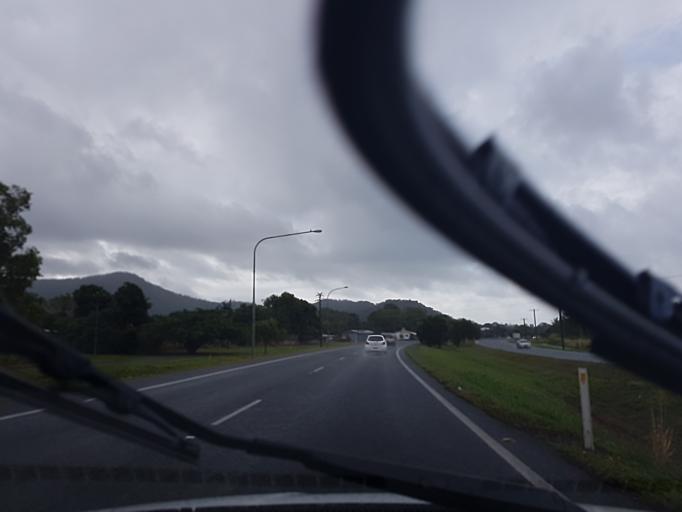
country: AU
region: Queensland
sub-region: Cairns
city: Yorkeys Knob
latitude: -16.8282
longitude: 145.6925
